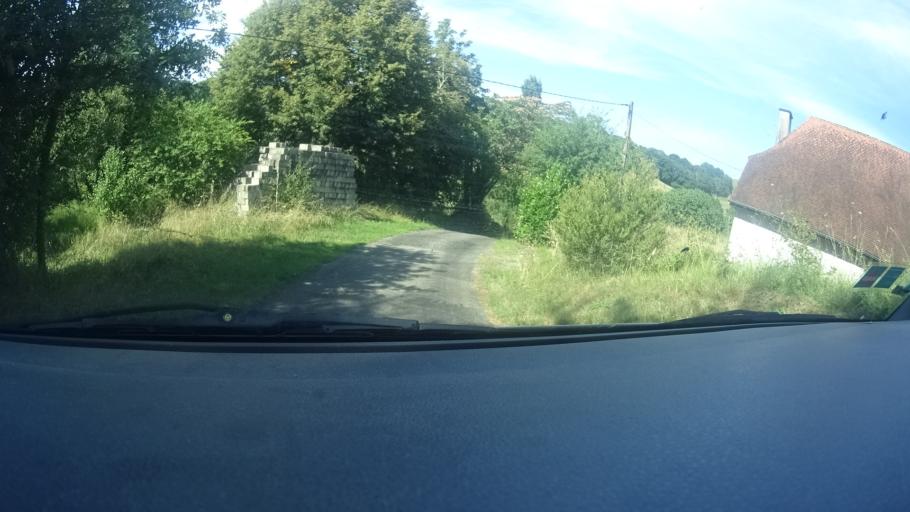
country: FR
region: Aquitaine
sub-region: Departement des Pyrenees-Atlantiques
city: Mont
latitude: 43.5013
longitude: -0.6921
